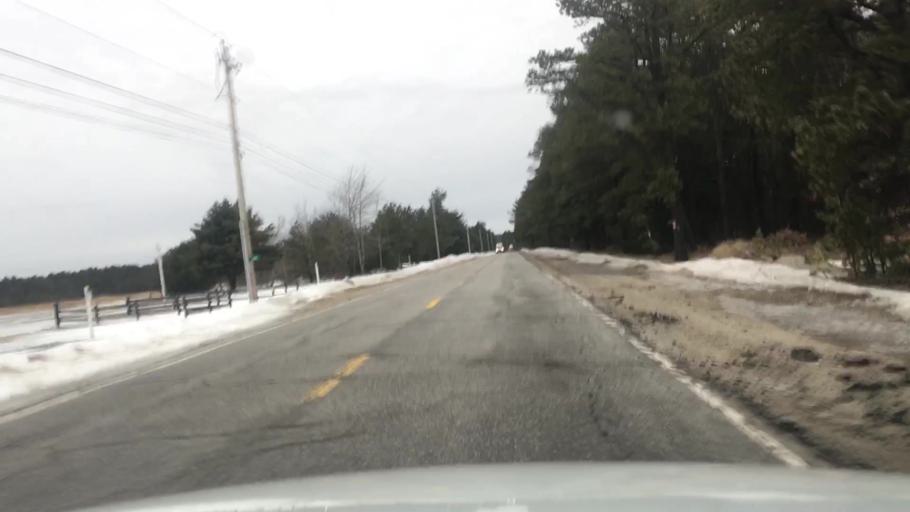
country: US
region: Maine
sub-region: York County
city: Shapleigh
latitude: 43.5908
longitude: -70.8779
